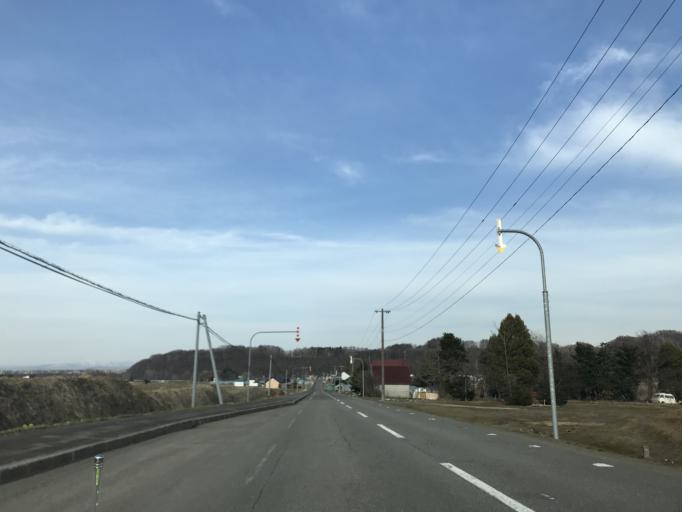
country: JP
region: Hokkaido
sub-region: Asahikawa-shi
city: Asahikawa
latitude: 43.7057
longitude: 142.3449
